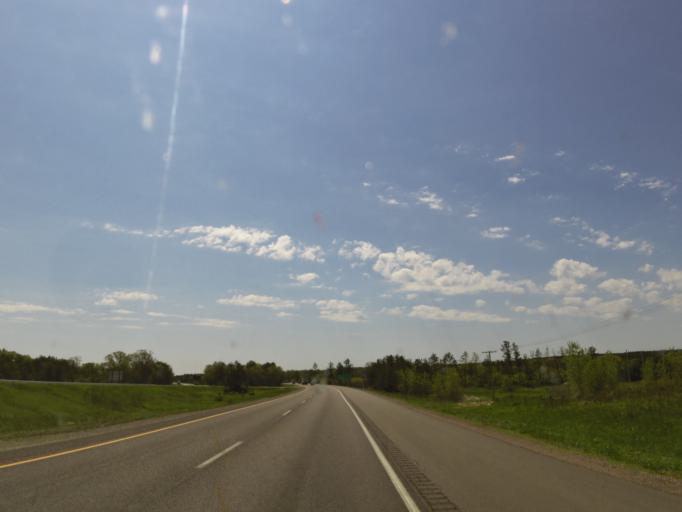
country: US
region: Wisconsin
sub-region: Trempealeau County
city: Osseo
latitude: 44.5738
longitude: -91.2012
